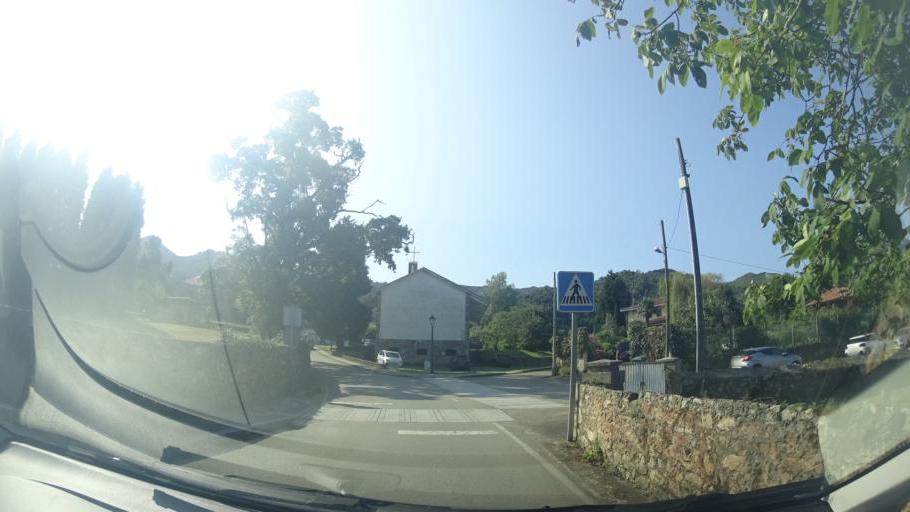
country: ES
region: Asturias
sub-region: Province of Asturias
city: Colunga
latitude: 43.4644
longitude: -5.1874
